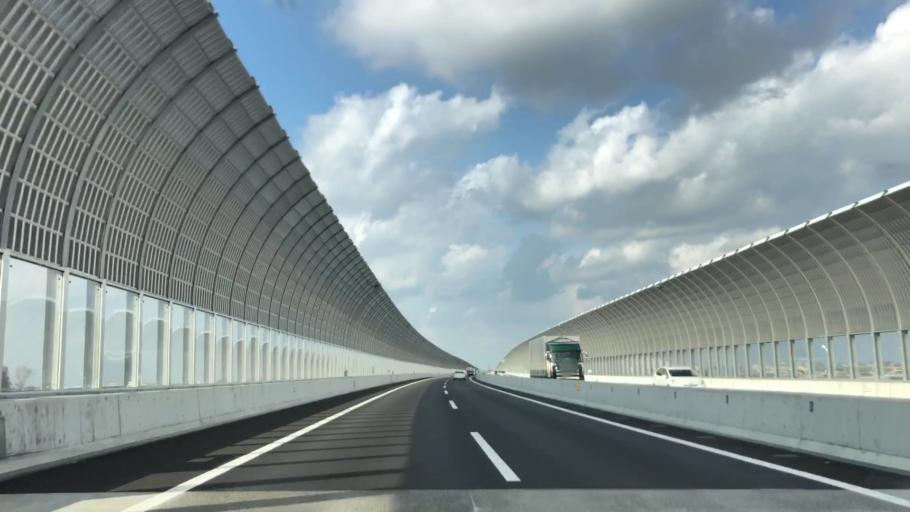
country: JP
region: Chiba
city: Matsudo
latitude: 35.7916
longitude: 139.8794
